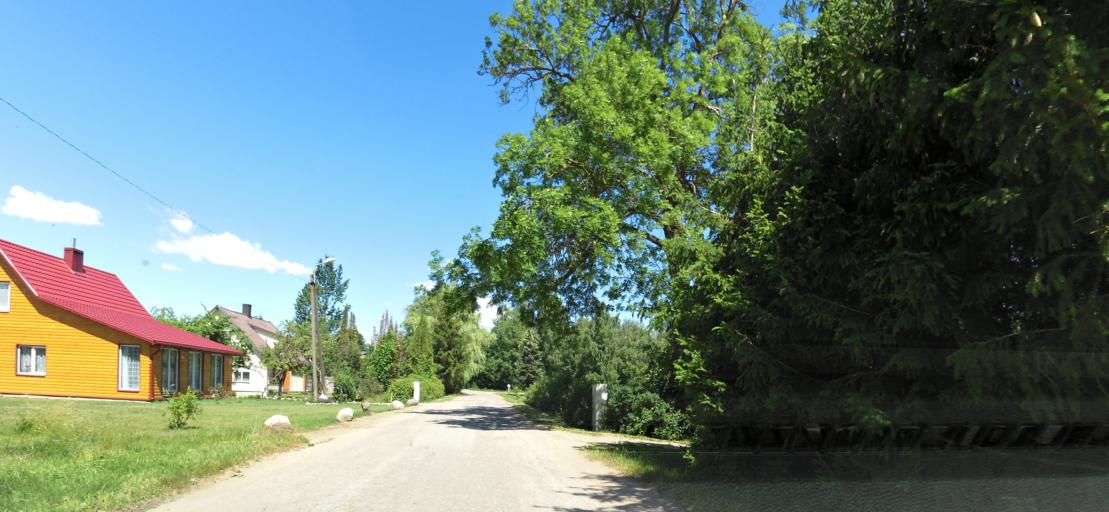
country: LT
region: Panevezys
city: Pasvalys
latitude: 56.2240
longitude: 24.5175
